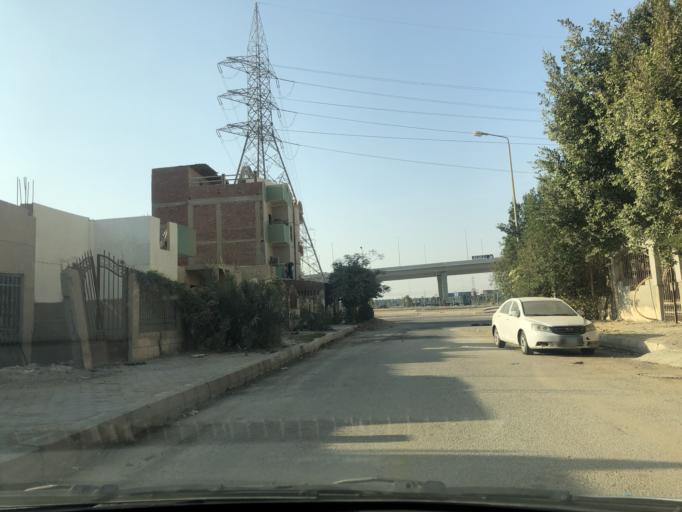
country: EG
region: Al Jizah
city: Madinat Sittah Uktubar
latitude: 29.9085
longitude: 30.9305
